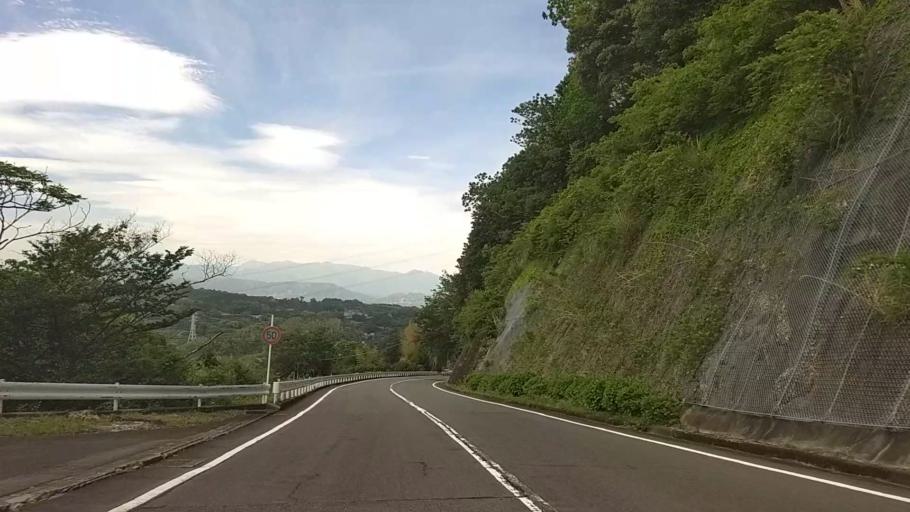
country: JP
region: Kanagawa
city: Odawara
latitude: 35.2383
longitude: 139.1278
